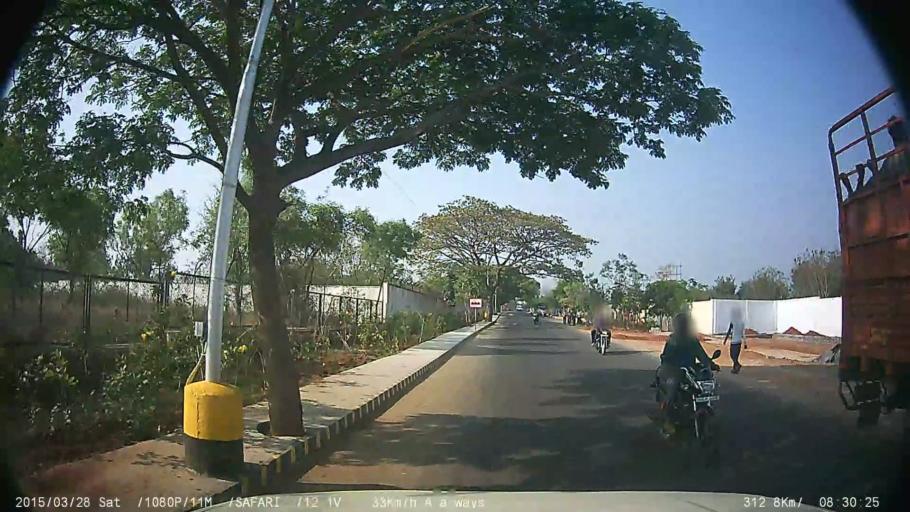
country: IN
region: Karnataka
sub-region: Mysore
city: Mysore
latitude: 12.3606
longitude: 76.6047
